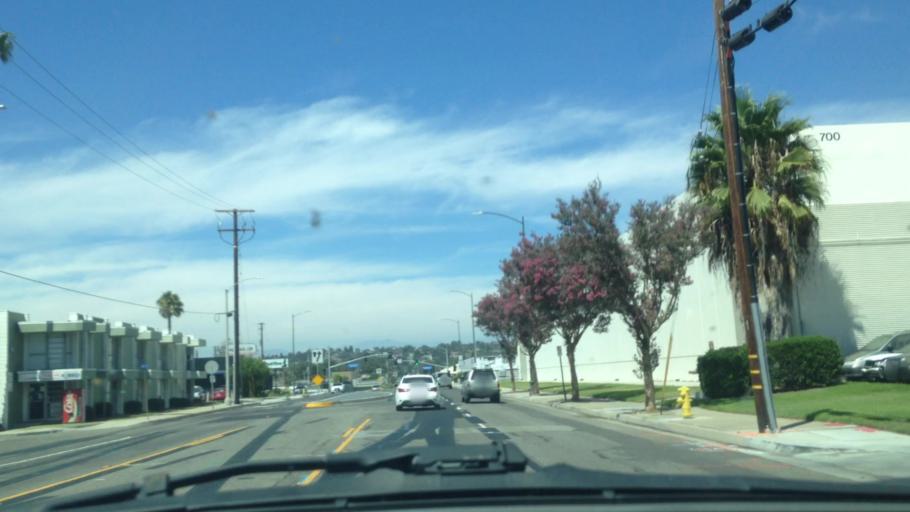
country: US
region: California
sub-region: Orange County
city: Fullerton
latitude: 33.8637
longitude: -117.9068
